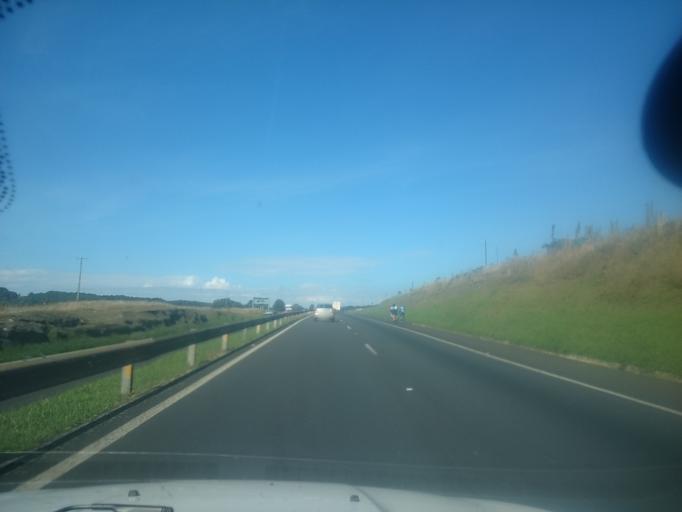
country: BR
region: Parana
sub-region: Campo Largo
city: Campo Largo
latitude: -25.4479
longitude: -49.7407
